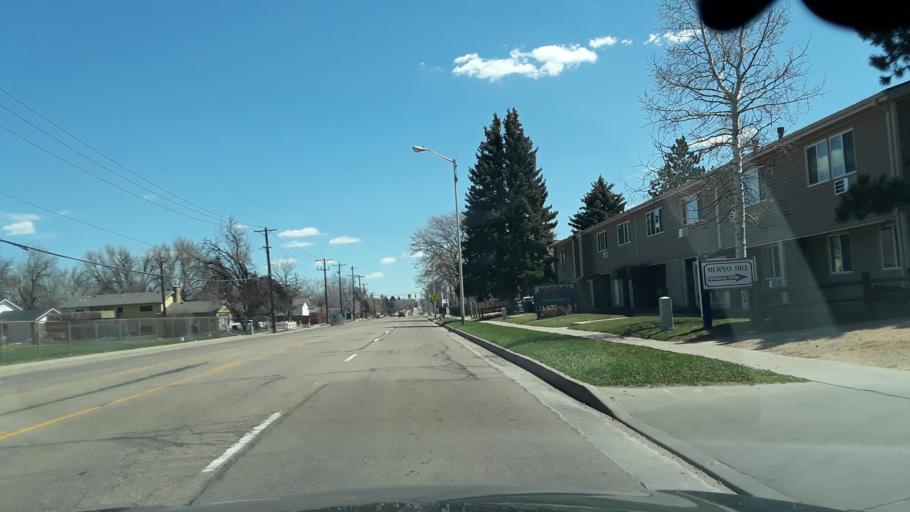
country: US
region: Colorado
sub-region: El Paso County
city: Cimarron Hills
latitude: 38.8471
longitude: -104.7504
